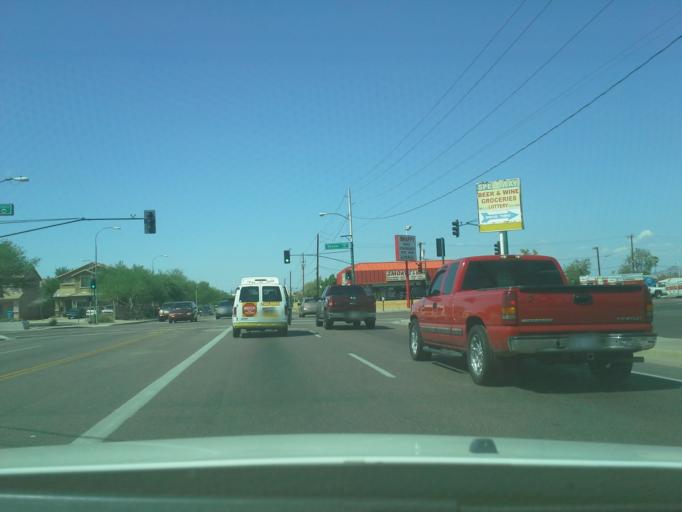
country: US
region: Arizona
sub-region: Maricopa County
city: Phoenix
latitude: 33.3991
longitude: -112.0646
